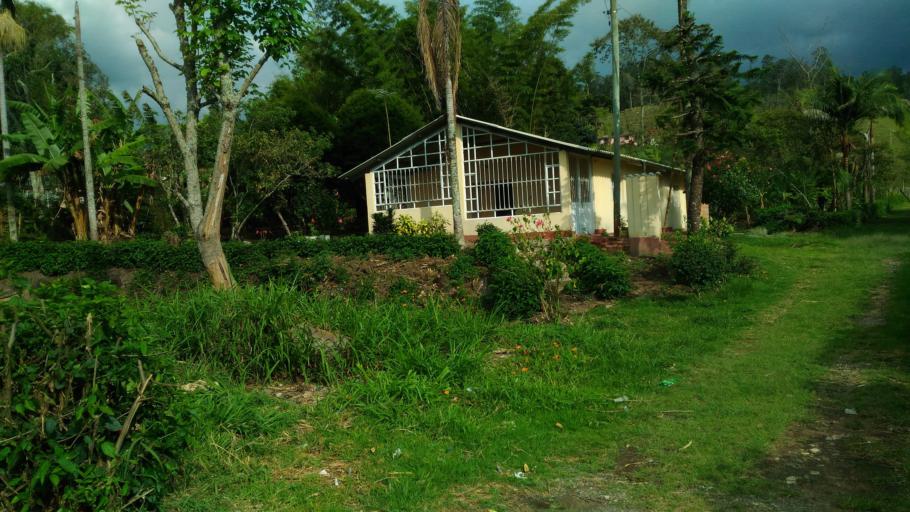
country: CO
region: Cundinamarca
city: Pacho
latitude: 5.1579
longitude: -74.1295
